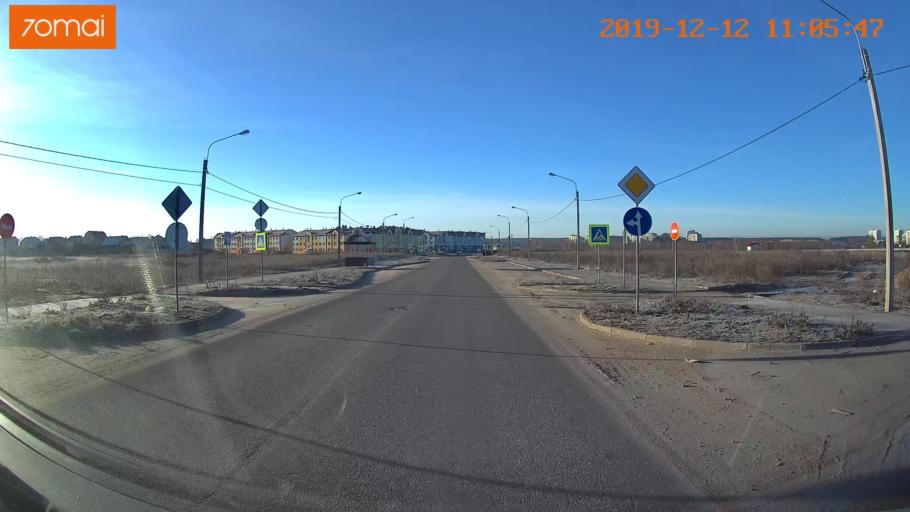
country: RU
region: Ivanovo
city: Kokhma
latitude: 56.9473
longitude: 41.0939
